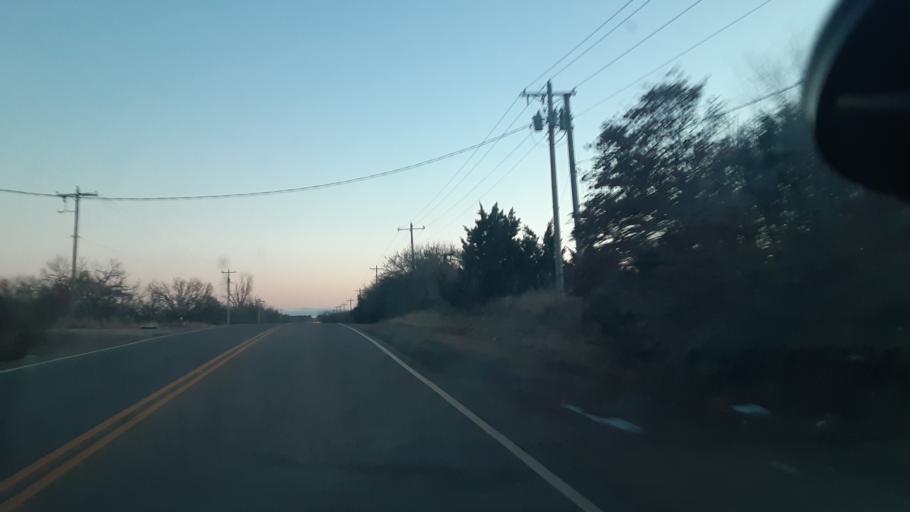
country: US
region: Oklahoma
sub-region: Oklahoma County
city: Edmond
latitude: 35.7012
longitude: -97.4252
